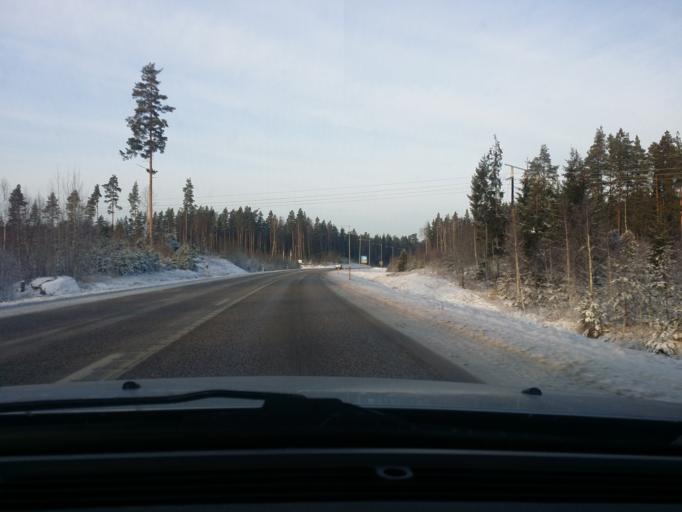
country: SE
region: OErebro
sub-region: Lindesbergs Kommun
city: Frovi
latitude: 59.4775
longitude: 15.3845
